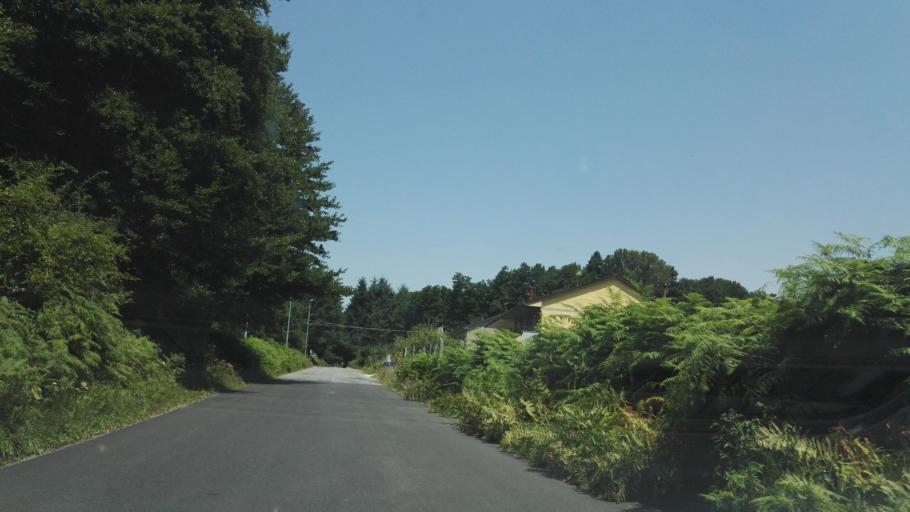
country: IT
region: Calabria
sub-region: Provincia di Vibo-Valentia
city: Mongiana
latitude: 38.5279
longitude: 16.3207
